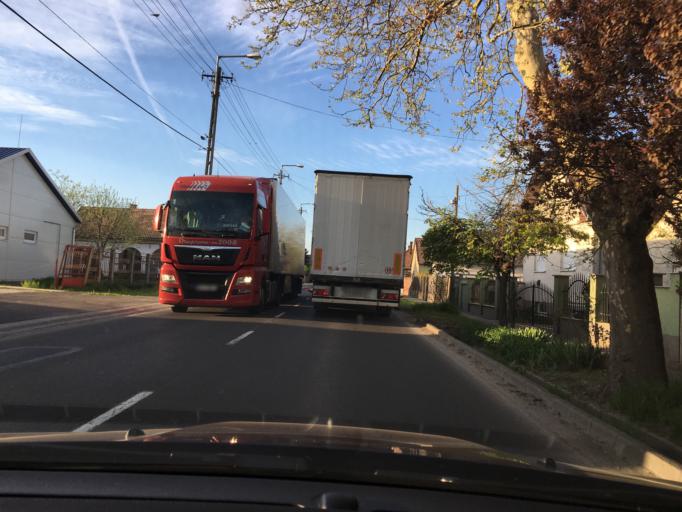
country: HU
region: Hajdu-Bihar
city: Mikepercs
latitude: 47.4452
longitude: 21.6320
